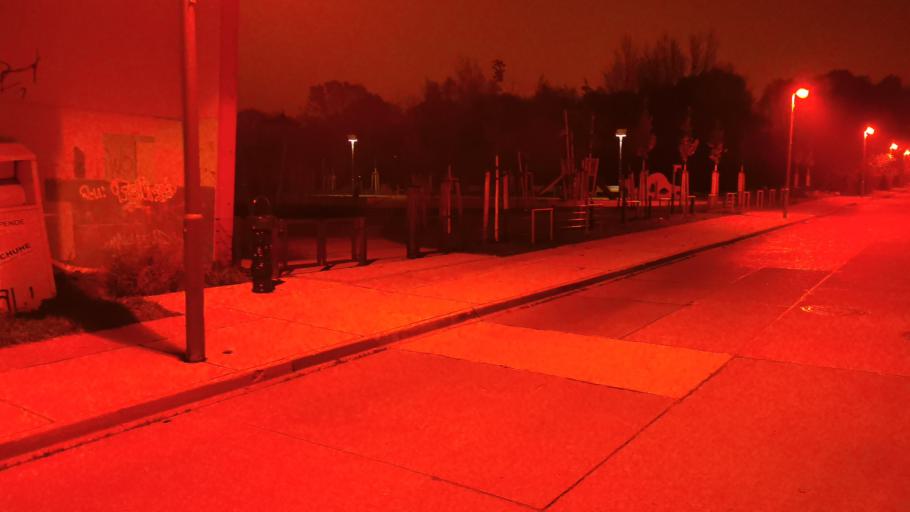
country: DE
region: Berlin
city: Marzahn
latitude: 52.5489
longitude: 13.5703
